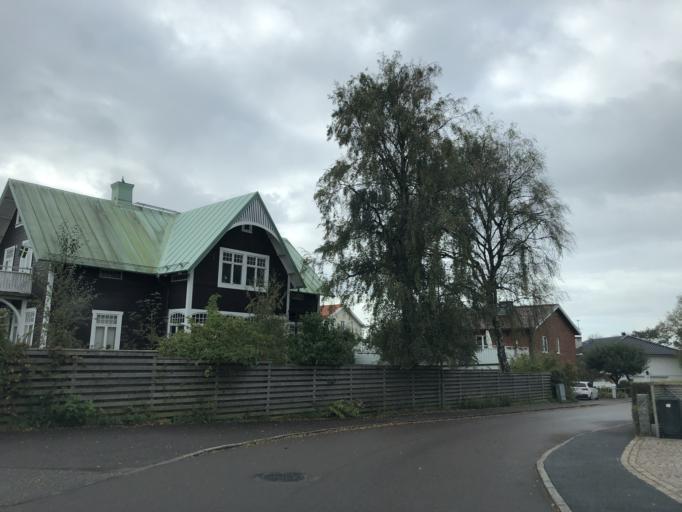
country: SE
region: Vaestra Goetaland
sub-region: Goteborg
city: Majorna
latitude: 57.6697
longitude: 11.8596
